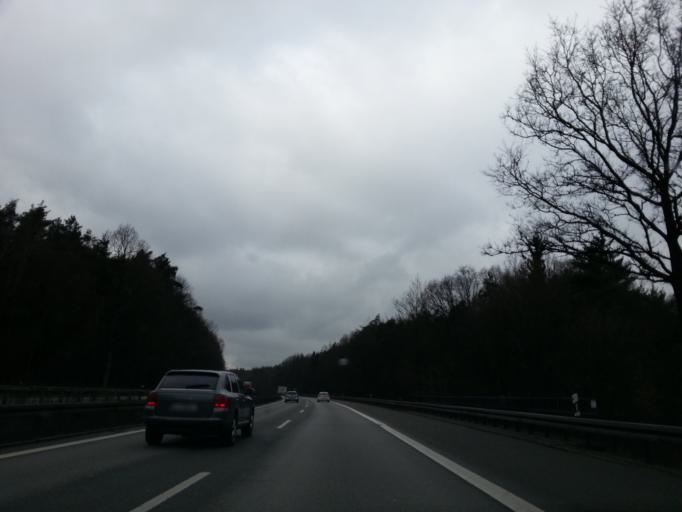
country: DE
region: Bavaria
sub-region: Upper Palatinate
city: Sinzing
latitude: 49.0040
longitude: 12.0020
